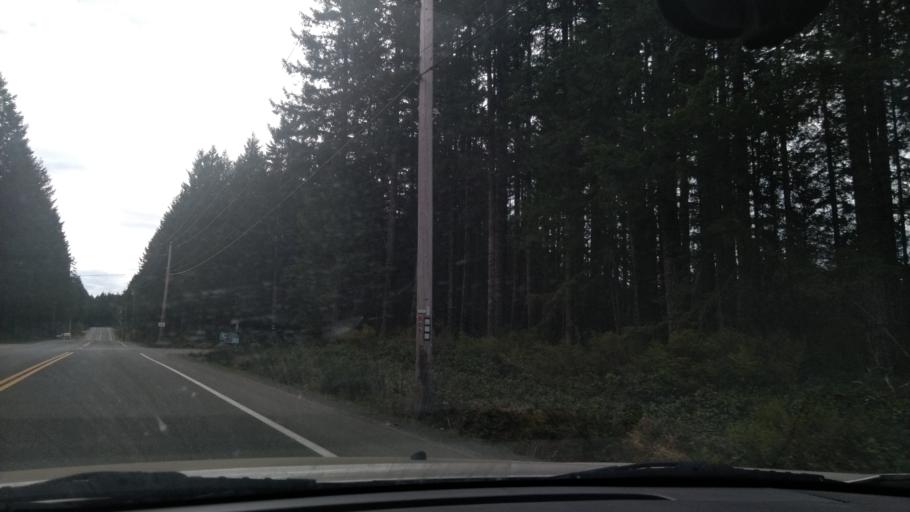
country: CA
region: British Columbia
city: Campbell River
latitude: 50.0153
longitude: -125.3550
